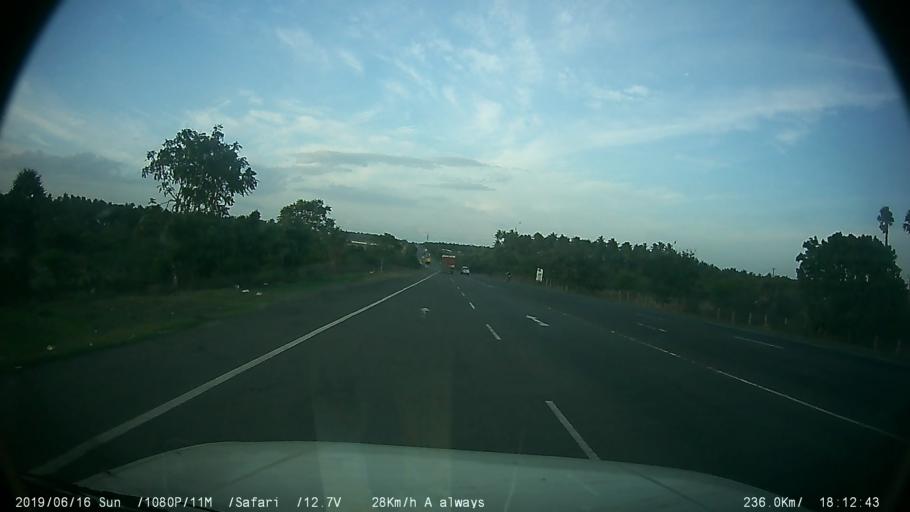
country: IN
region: Tamil Nadu
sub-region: Coimbatore
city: Madukkarai
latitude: 10.9215
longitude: 76.9895
